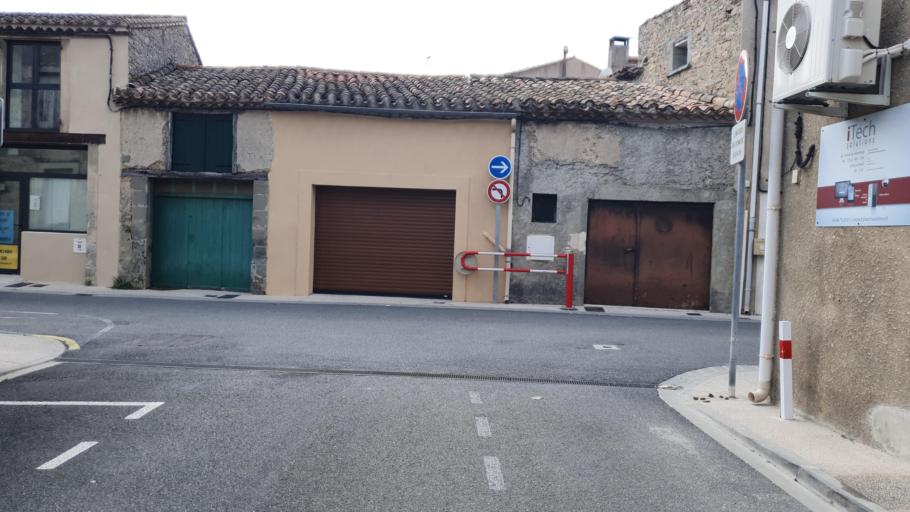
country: FR
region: Languedoc-Roussillon
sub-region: Departement de l'Aude
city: Bram
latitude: 43.2423
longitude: 2.1137
